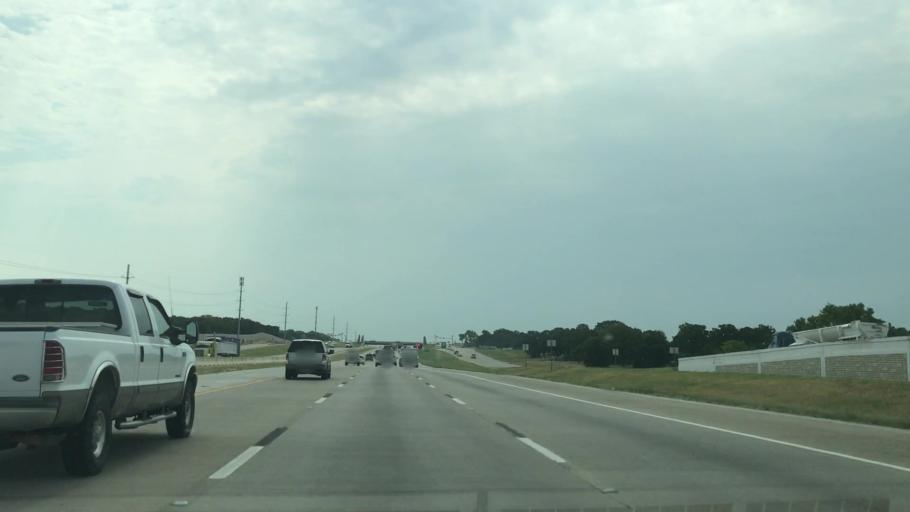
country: US
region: Texas
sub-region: Denton County
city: Trophy Club
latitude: 32.9915
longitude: -97.1897
